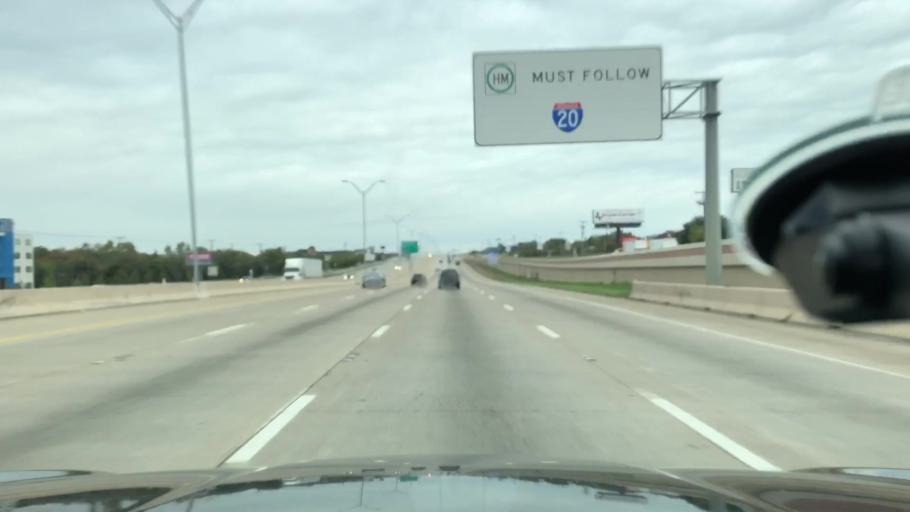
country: US
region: Texas
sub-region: Dallas County
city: DeSoto
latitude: 32.6103
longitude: -96.8229
